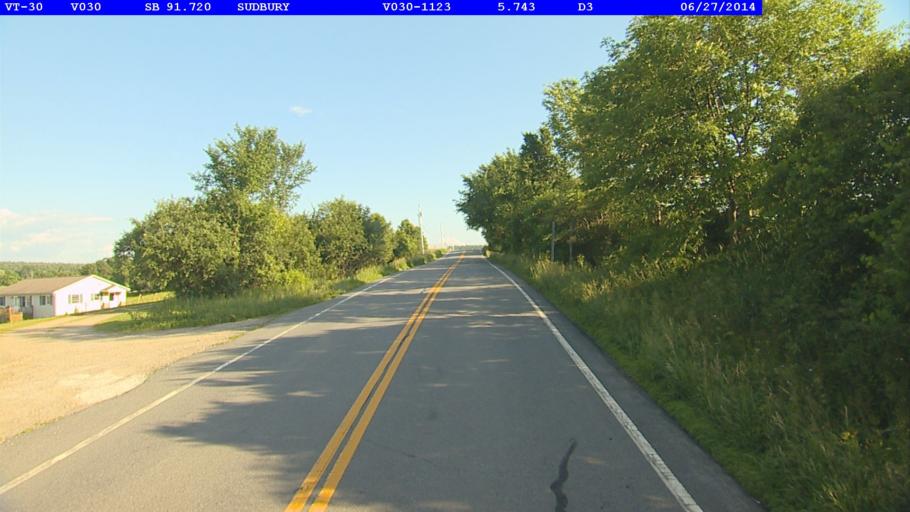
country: US
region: Vermont
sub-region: Rutland County
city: Brandon
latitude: 43.8288
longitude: -73.1934
